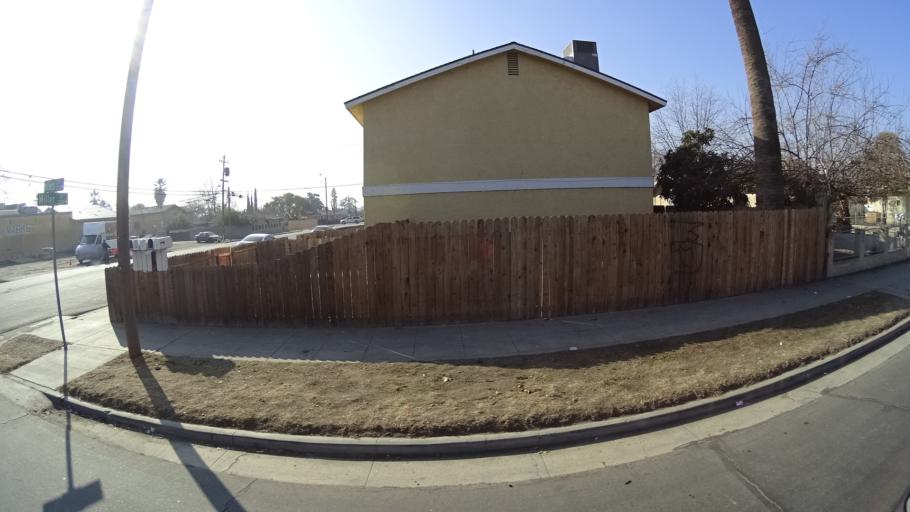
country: US
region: California
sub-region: Kern County
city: Bakersfield
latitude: 35.3798
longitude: -118.9819
